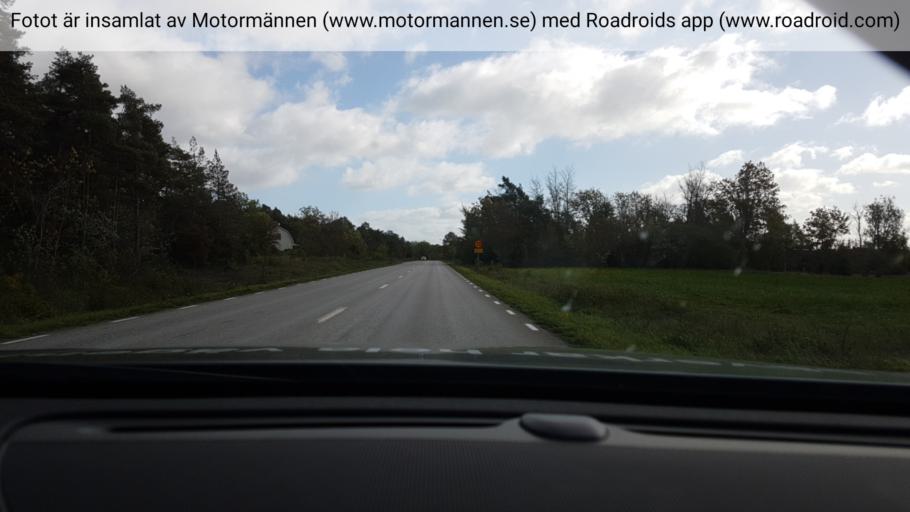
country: SE
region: Gotland
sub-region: Gotland
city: Slite
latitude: 57.8568
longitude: 19.0081
